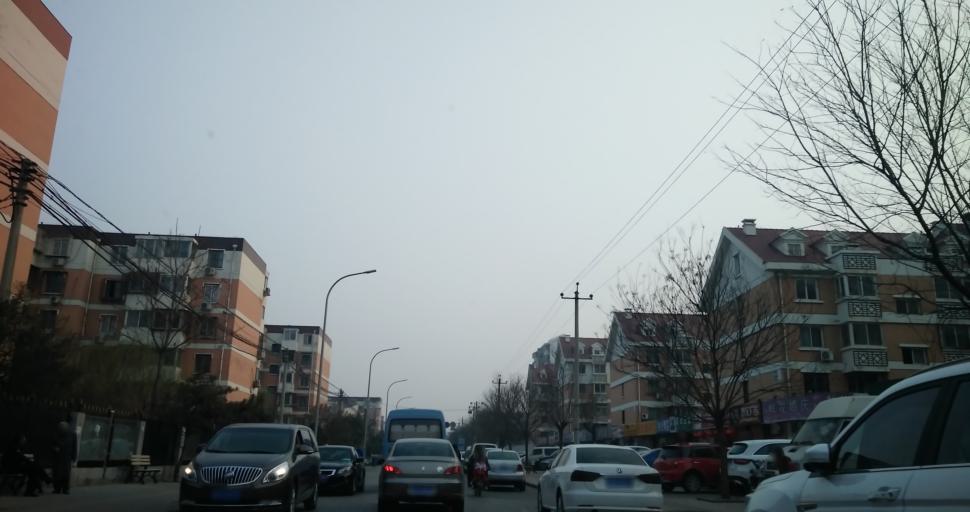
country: CN
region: Beijing
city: Xingfeng
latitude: 39.7299
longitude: 116.3425
